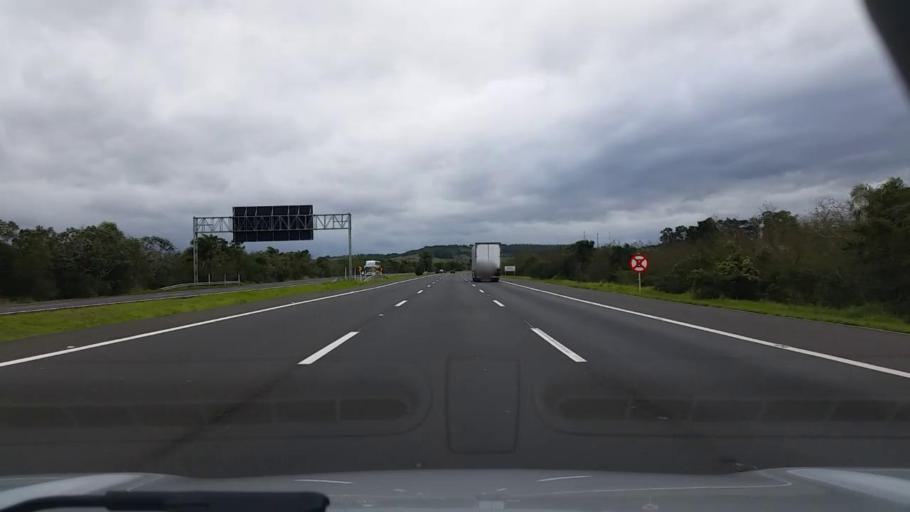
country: BR
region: Rio Grande do Sul
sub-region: Osorio
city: Osorio
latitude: -29.8880
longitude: -50.4565
